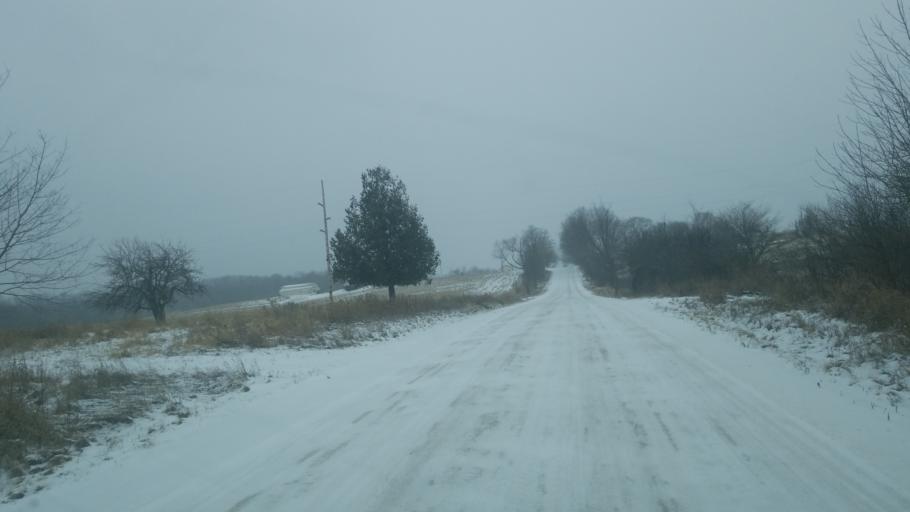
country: US
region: Michigan
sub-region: Osceola County
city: Reed City
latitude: 43.8335
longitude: -85.3939
